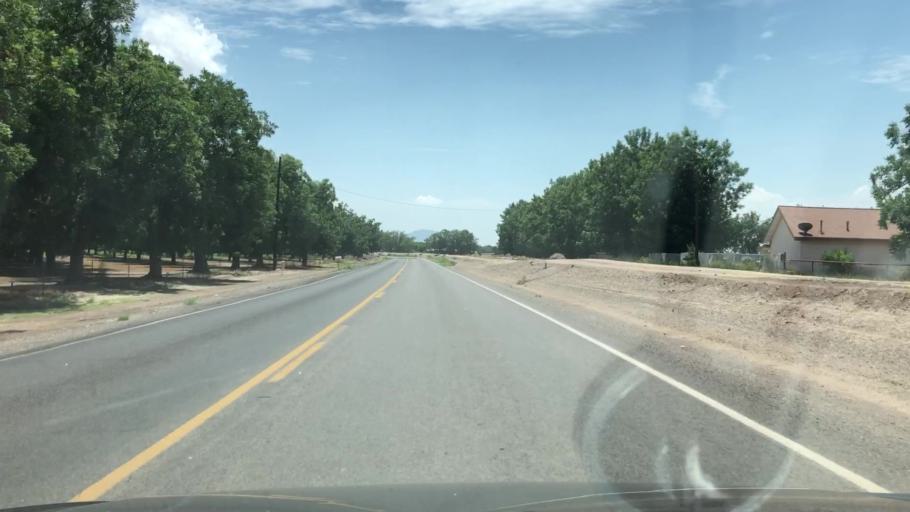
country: US
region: New Mexico
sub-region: Dona Ana County
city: La Union
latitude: 32.0060
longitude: -106.6621
